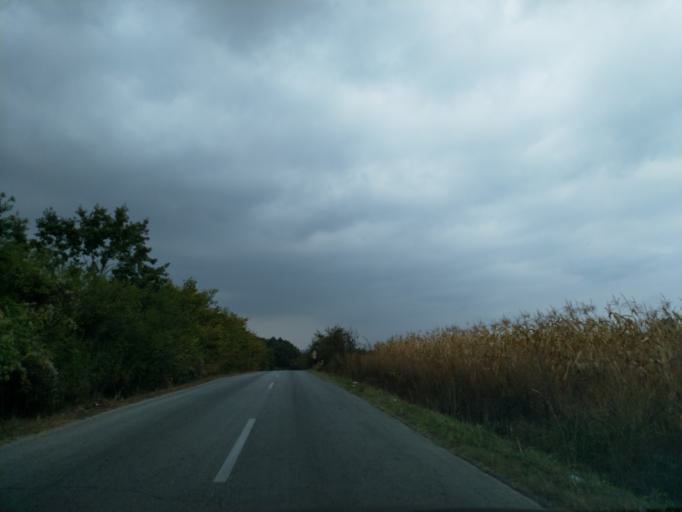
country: RS
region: Central Serbia
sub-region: Pomoravski Okrug
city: Jagodina
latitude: 44.0204
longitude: 21.1961
